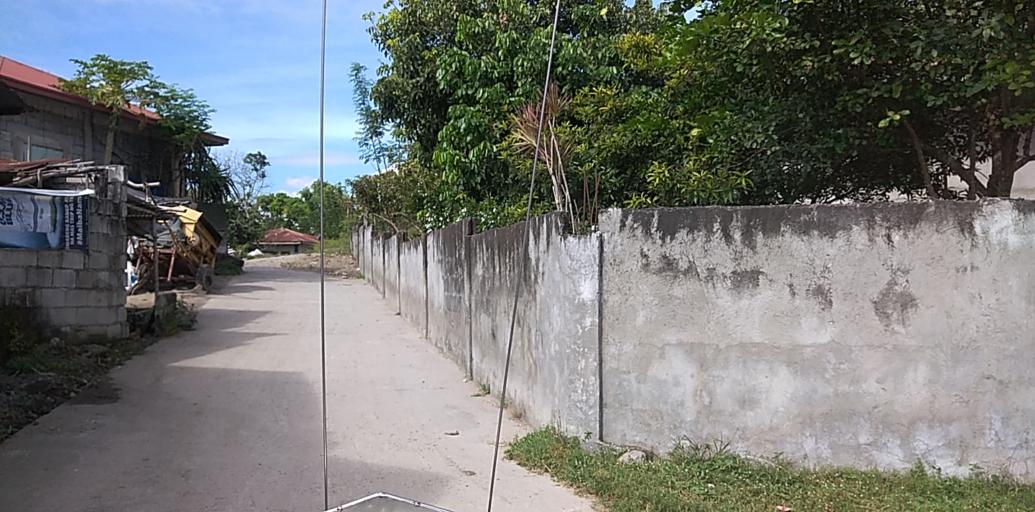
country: PH
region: Central Luzon
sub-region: Province of Pampanga
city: Porac
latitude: 15.0778
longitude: 120.5339
